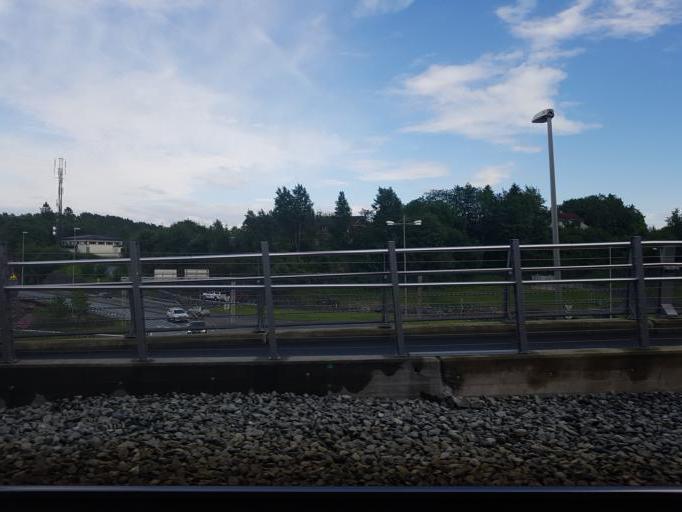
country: NO
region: Hordaland
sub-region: Bergen
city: Ytrebygda
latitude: 60.2891
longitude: 5.2635
